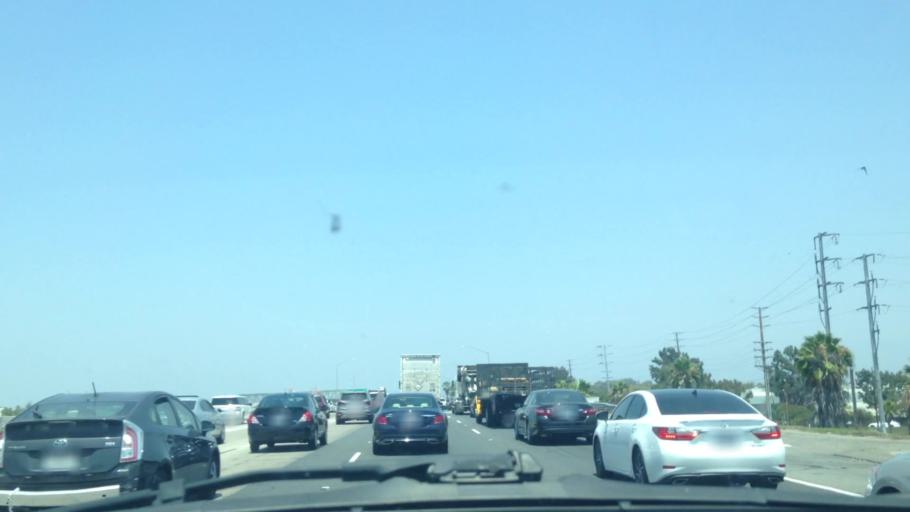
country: US
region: California
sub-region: Orange County
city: Irvine
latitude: 33.6977
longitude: -117.8621
